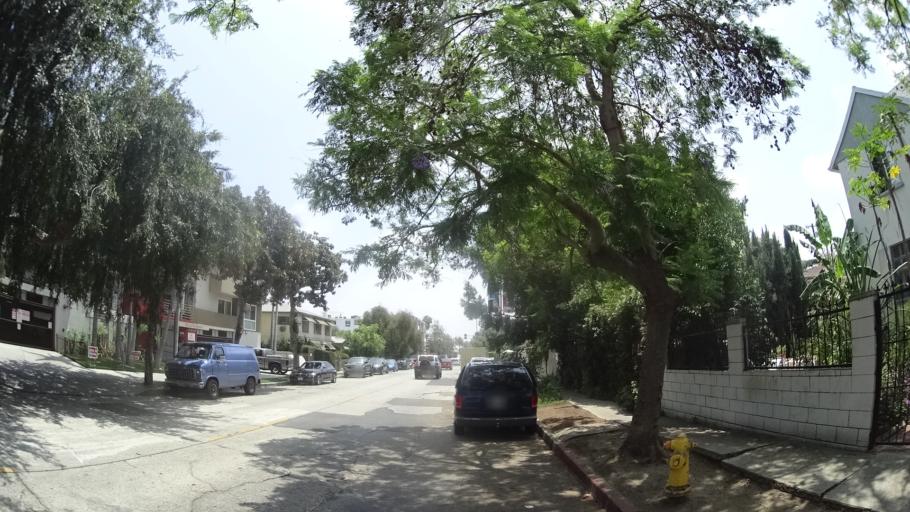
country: US
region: California
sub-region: Los Angeles County
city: Hollywood
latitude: 34.0881
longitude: -118.3311
